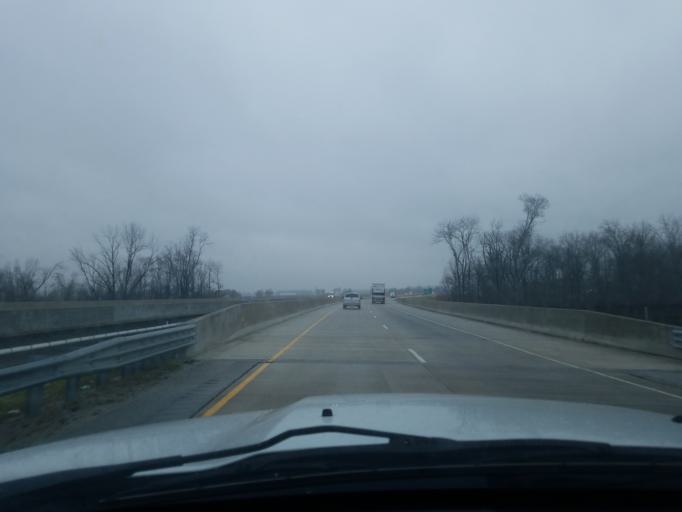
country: US
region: Indiana
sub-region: Howard County
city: Indian Heights
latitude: 40.4418
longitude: -86.0771
